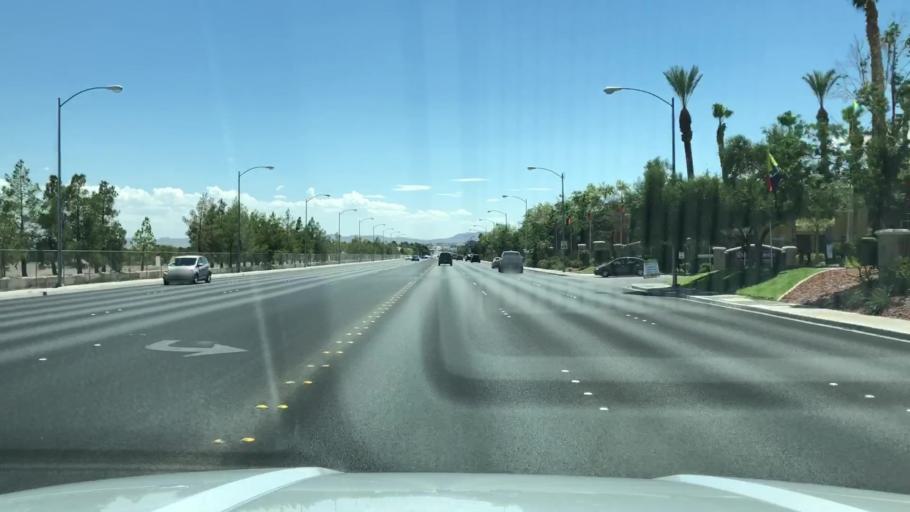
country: US
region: Nevada
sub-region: Clark County
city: Spring Valley
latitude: 36.1070
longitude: -115.2792
